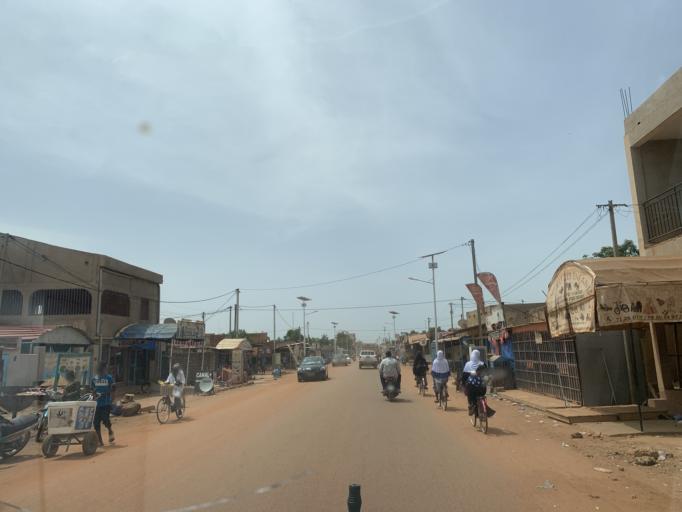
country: BF
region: Centre
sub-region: Kadiogo Province
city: Ouagadougou
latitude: 12.3321
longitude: -1.4928
